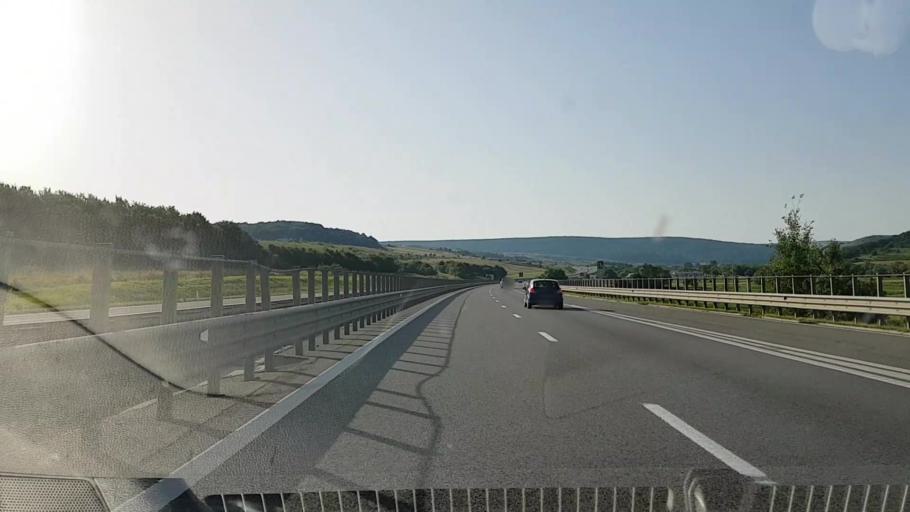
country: RO
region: Cluj
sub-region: Comuna Savadisla
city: Savadisla
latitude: 46.6992
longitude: 23.4366
